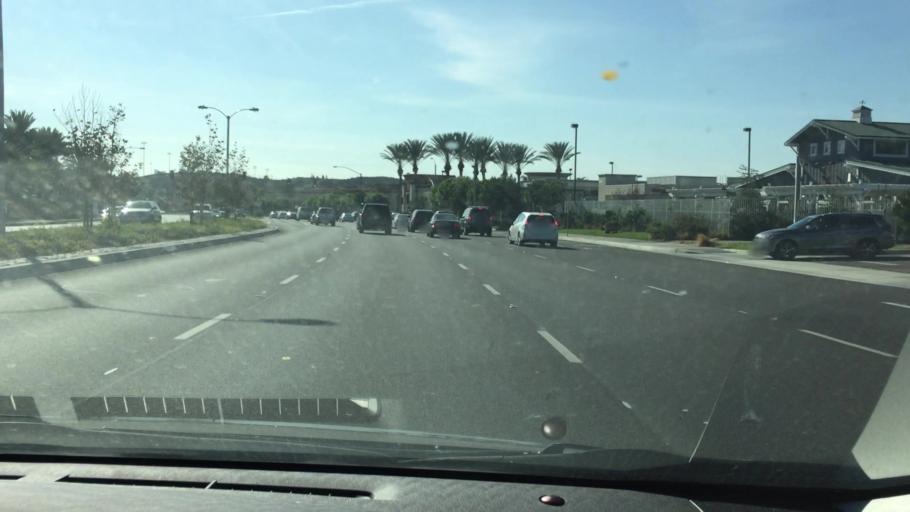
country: US
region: California
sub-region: Orange County
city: Foothill Ranch
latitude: 33.6637
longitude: -117.6531
